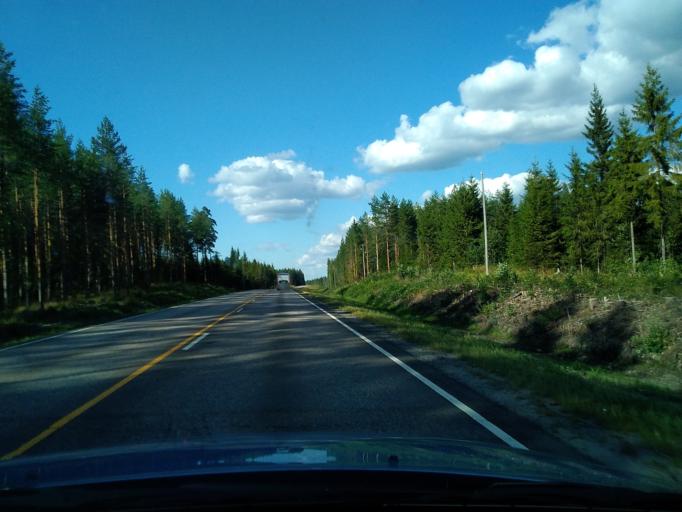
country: FI
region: Pirkanmaa
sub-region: Ylae-Pirkanmaa
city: Maenttae
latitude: 62.0782
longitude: 24.7253
